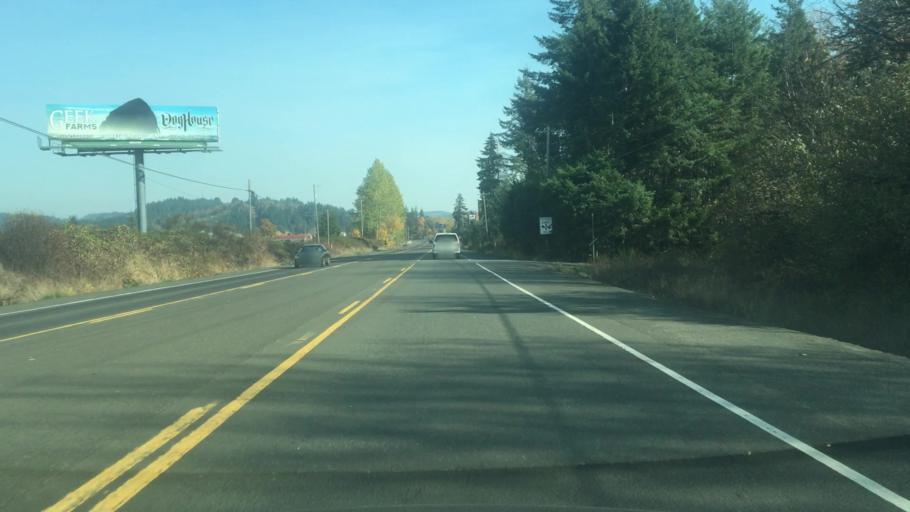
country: US
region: Oregon
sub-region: Polk County
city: Grand Ronde
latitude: 45.0583
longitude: -123.6238
